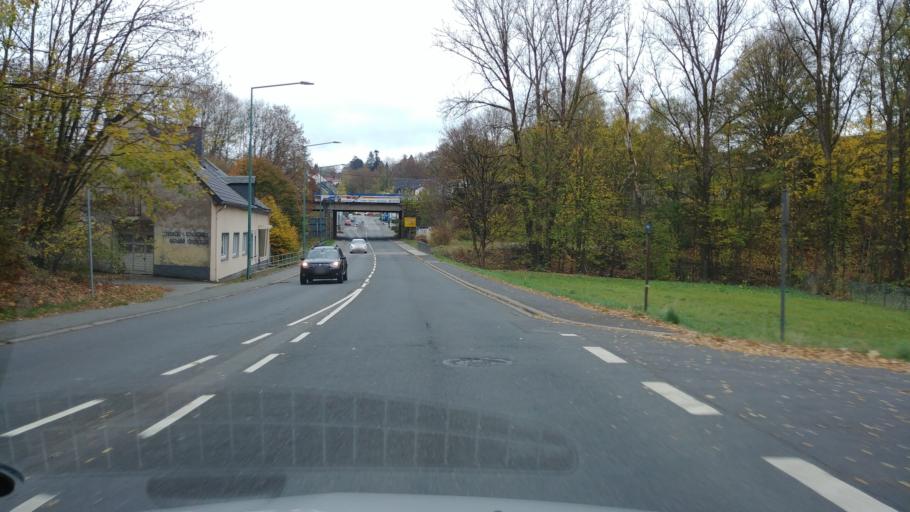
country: DE
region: Rheinland-Pfalz
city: Hermeskeil
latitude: 49.6585
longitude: 6.9301
